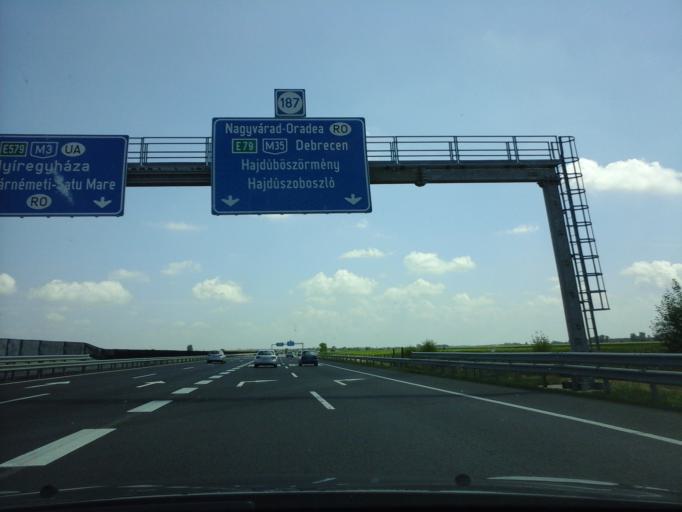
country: HU
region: Hajdu-Bihar
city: Gorbehaza
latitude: 47.7966
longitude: 21.2365
